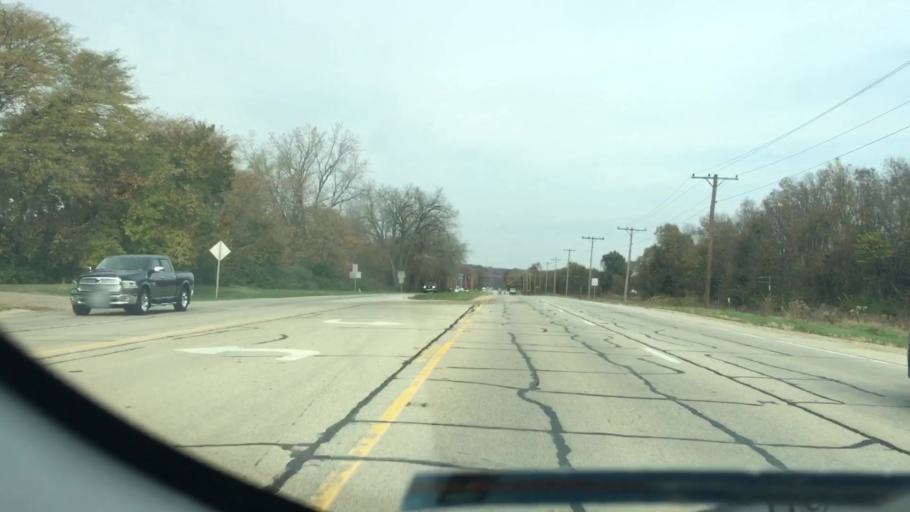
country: US
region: Illinois
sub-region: Peoria County
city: Peoria Heights
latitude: 40.7609
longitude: -89.5664
